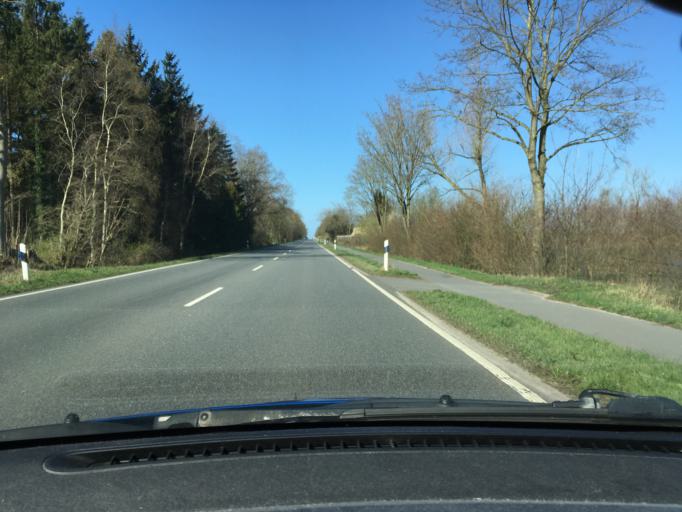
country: DE
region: Schleswig-Holstein
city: Geltorf
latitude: 54.4915
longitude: 9.6308
